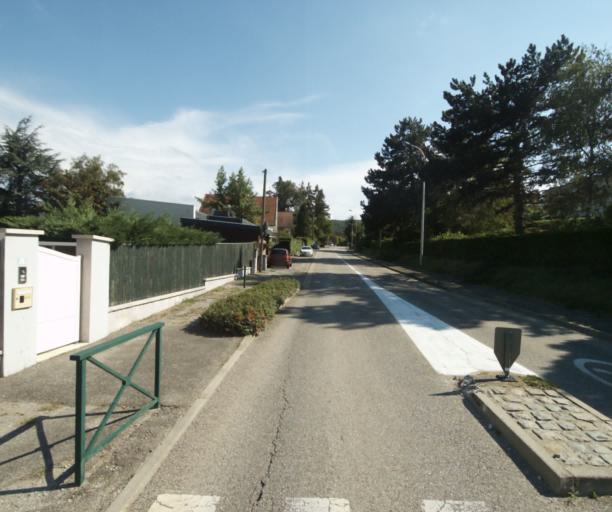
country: FR
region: Rhone-Alpes
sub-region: Departement de l'Isere
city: Seyssins
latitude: 45.1606
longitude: 5.6815
